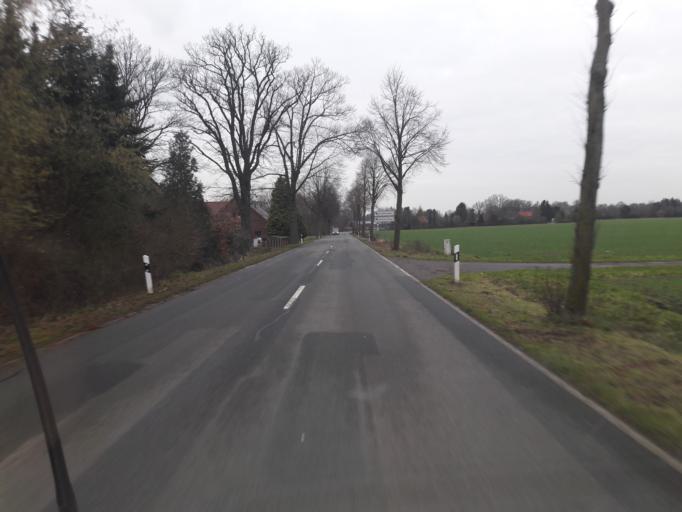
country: DE
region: Lower Saxony
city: Warmsen
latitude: 52.4470
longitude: 8.8547
